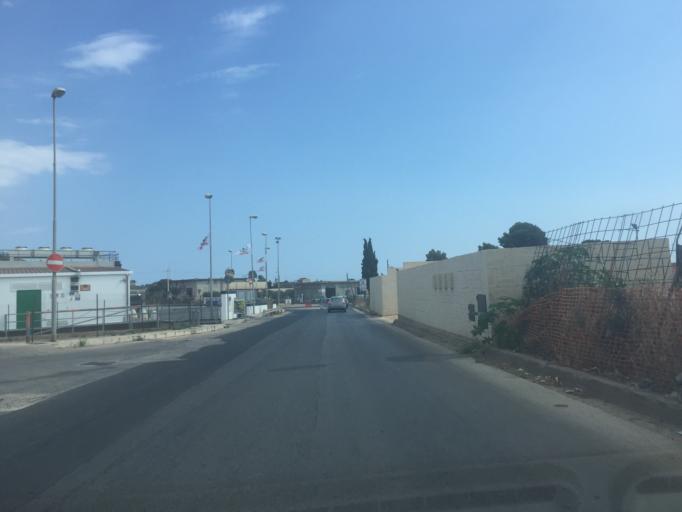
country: IT
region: Sicily
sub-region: Ragusa
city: Santa Croce Camerina
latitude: 36.8225
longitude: 14.5194
